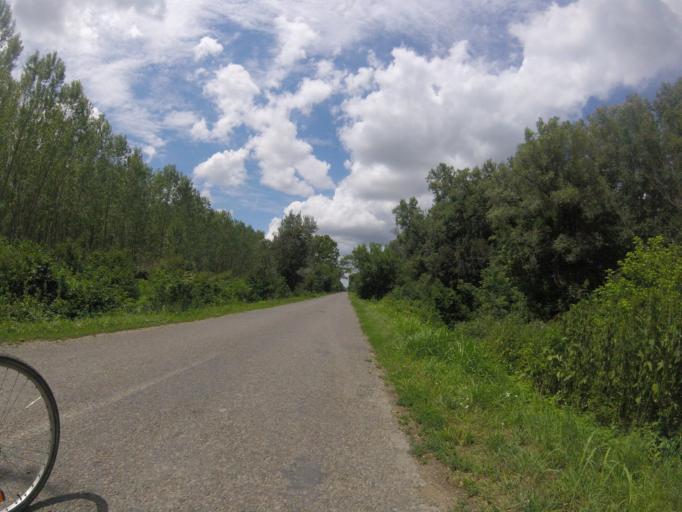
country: HU
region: Tolna
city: Bogyiszlo
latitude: 46.3297
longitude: 18.8404
